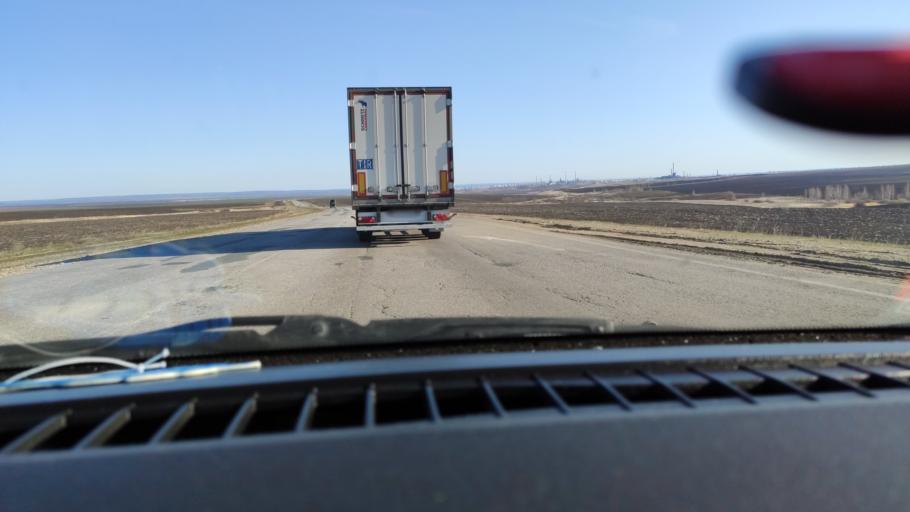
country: RU
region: Samara
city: Syzran'
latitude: 53.0053
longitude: 48.3317
